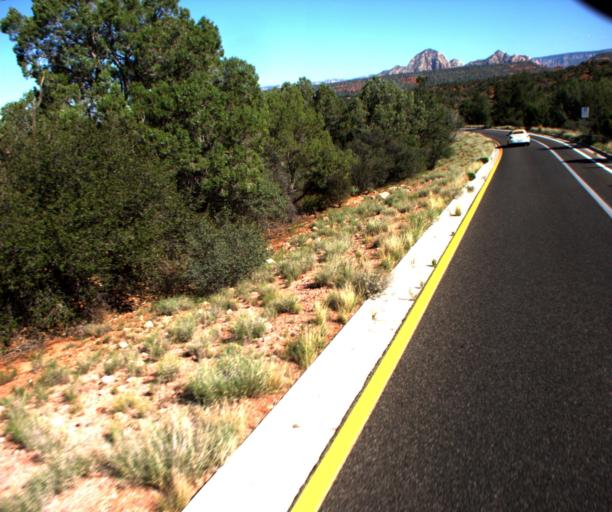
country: US
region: Arizona
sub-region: Yavapai County
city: Village of Oak Creek (Big Park)
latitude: 34.8153
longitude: -111.7665
